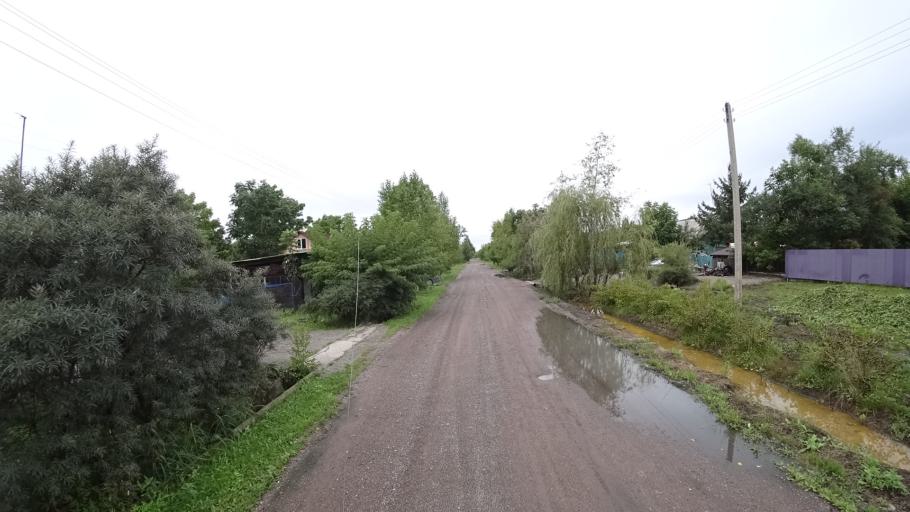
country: RU
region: Primorskiy
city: Monastyrishche
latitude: 44.1953
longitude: 132.4724
